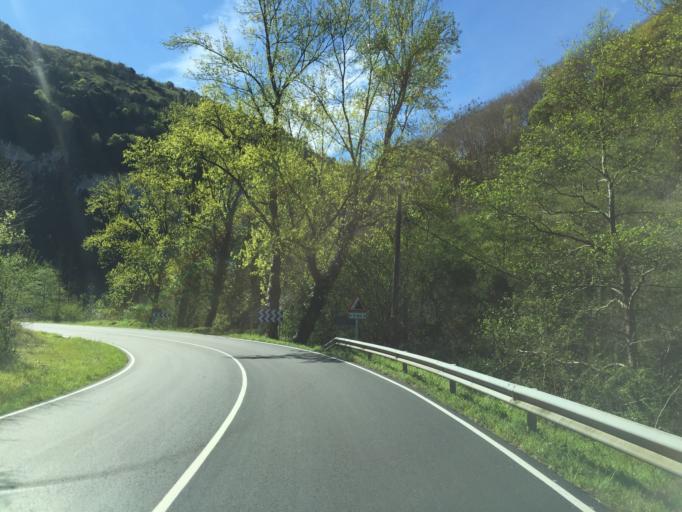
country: ES
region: Asturias
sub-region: Province of Asturias
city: Proaza
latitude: 43.3067
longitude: -5.9859
